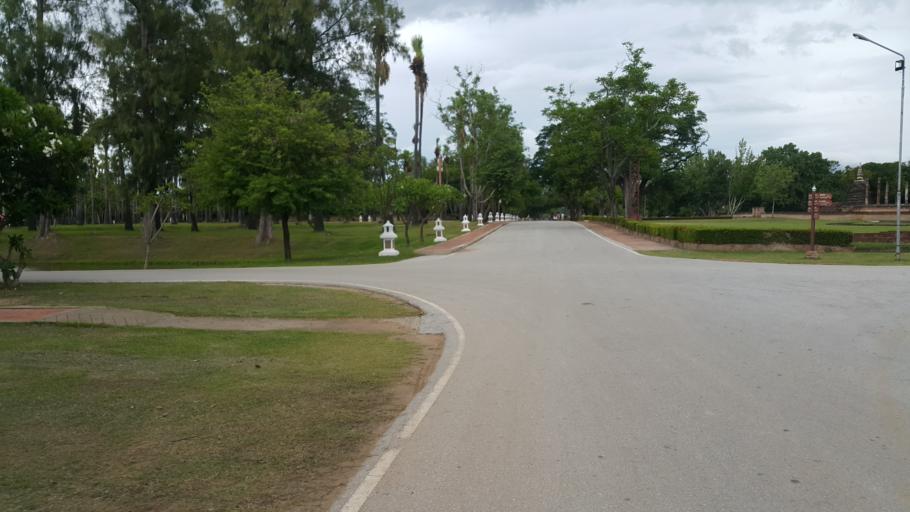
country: TH
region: Sukhothai
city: Ban Na
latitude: 17.0186
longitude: 99.7049
